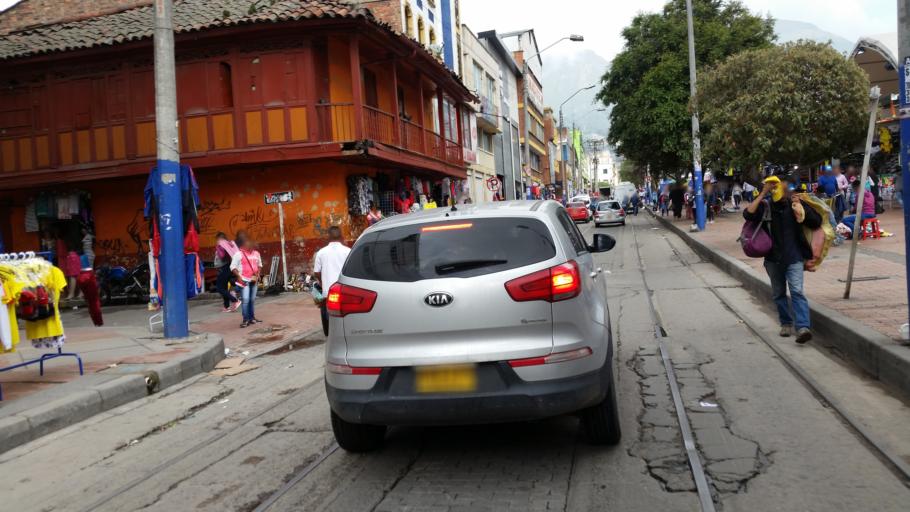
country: CO
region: Bogota D.C.
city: Bogota
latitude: 4.6003
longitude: -74.0805
